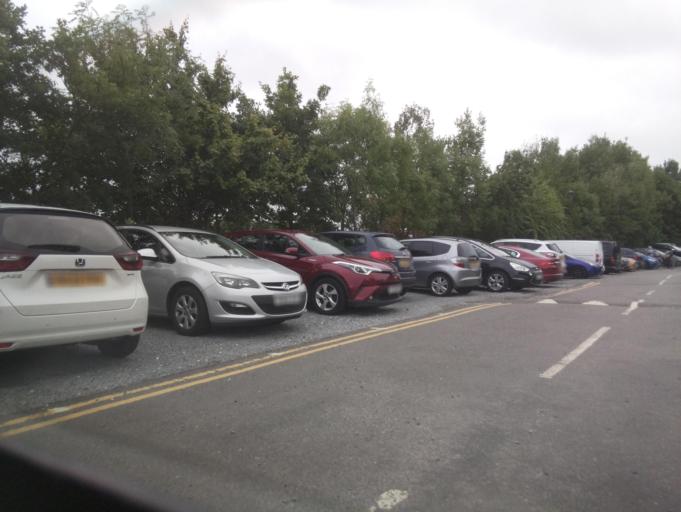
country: GB
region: England
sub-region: Derbyshire
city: Findern
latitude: 52.8596
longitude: -1.5544
